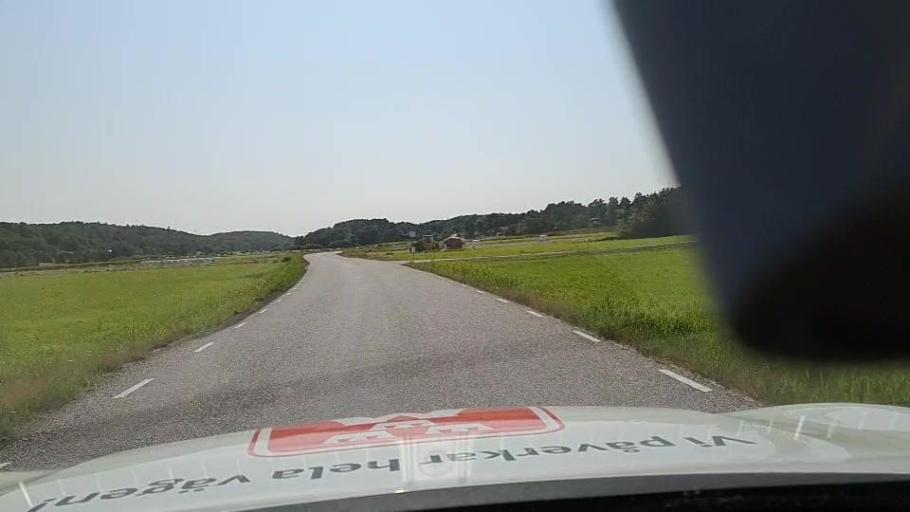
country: SE
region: Vaestra Goetaland
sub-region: Tjorns Kommun
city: Skaerhamn
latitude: 58.1275
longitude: 11.5536
